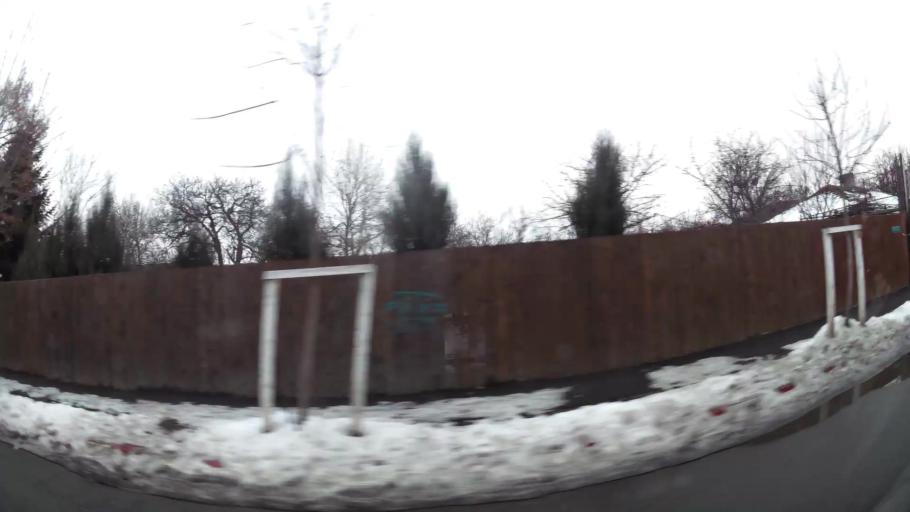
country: RO
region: Ilfov
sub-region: Voluntari City
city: Voluntari
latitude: 44.4845
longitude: 26.1692
